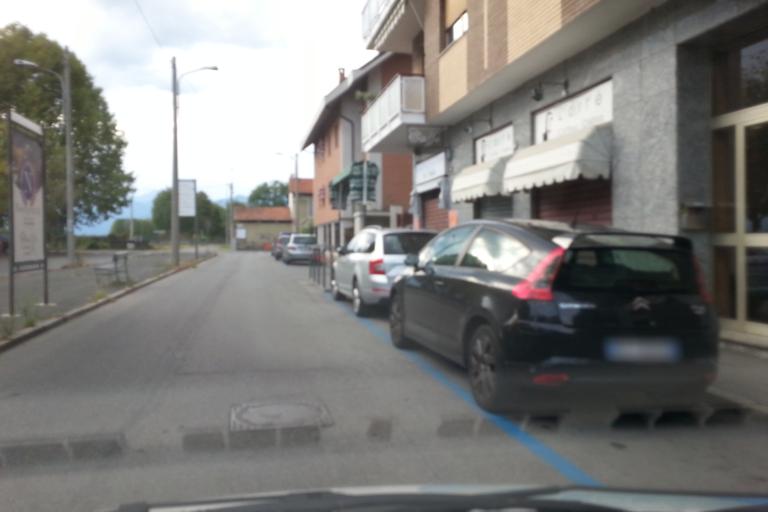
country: IT
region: Piedmont
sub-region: Provincia di Torino
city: Venaria Reale
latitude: 45.1299
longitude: 7.6233
